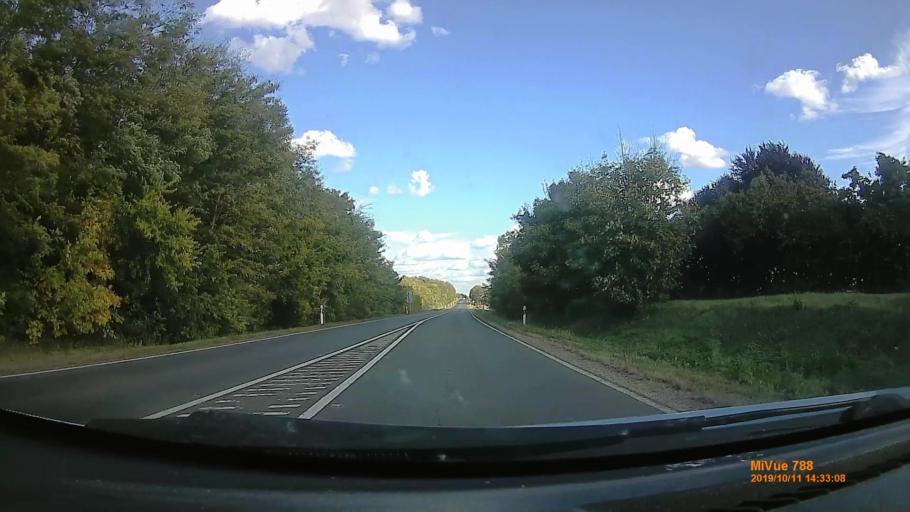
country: HU
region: Hajdu-Bihar
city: Ebes
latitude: 47.5622
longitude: 21.4507
